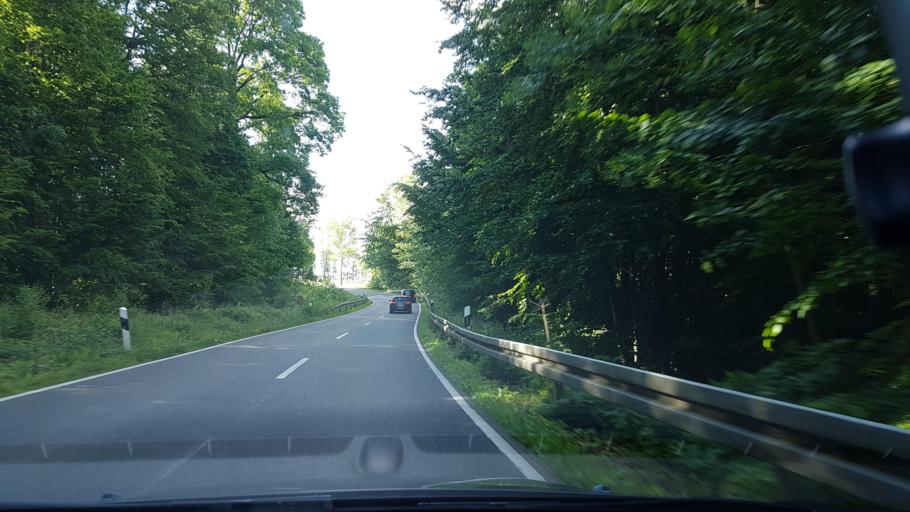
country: DE
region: Lower Saxony
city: Elze
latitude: 52.1311
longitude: 9.6731
